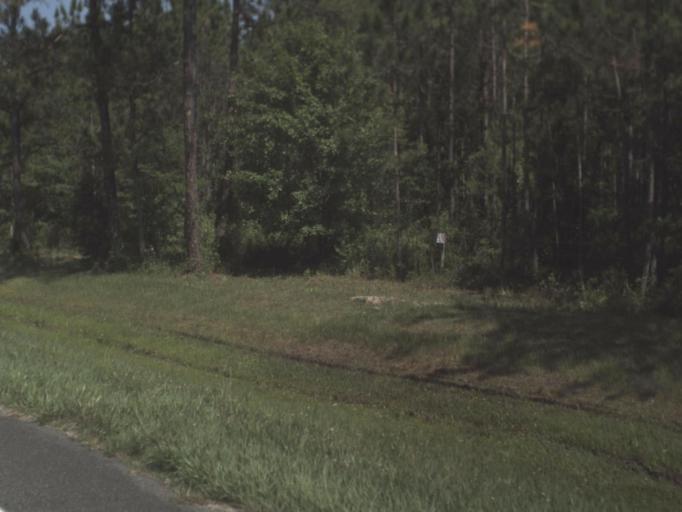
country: US
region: Florida
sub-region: Clay County
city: Asbury Lake
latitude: 29.9829
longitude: -81.7782
